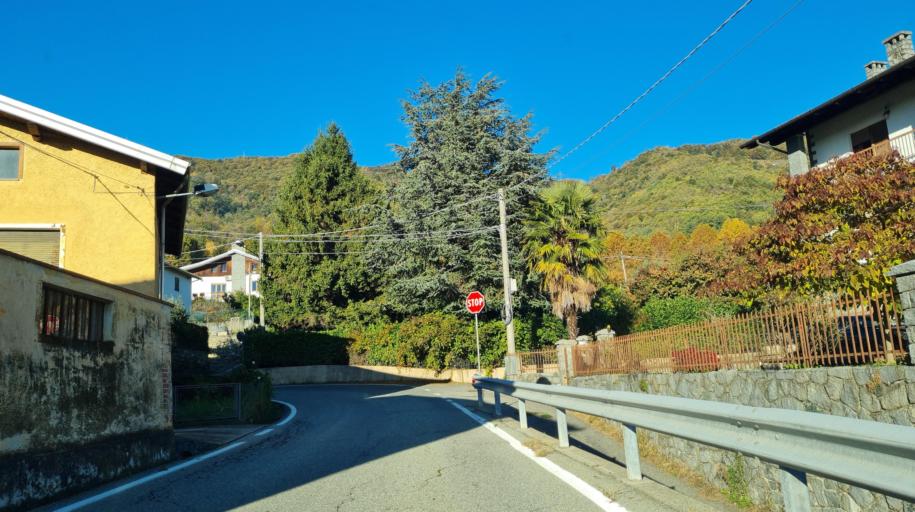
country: IT
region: Piedmont
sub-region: Provincia di Torino
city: Lessolo
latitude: 45.4755
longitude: 7.8105
